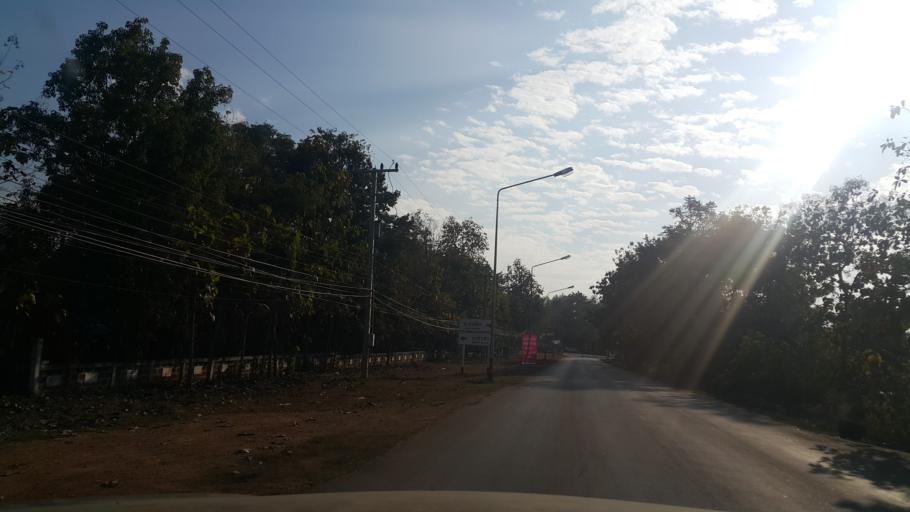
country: TH
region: Lampang
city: Ko Kha
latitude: 18.2158
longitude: 99.3403
